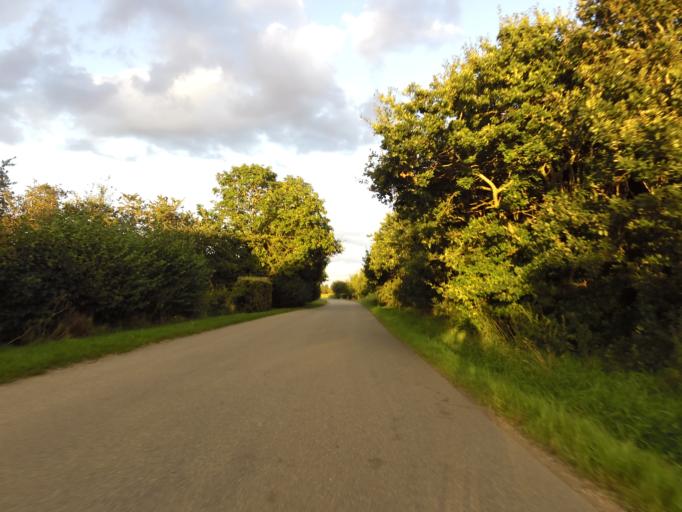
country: DK
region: South Denmark
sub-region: Tonder Kommune
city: Sherrebek
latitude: 55.2409
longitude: 8.8687
